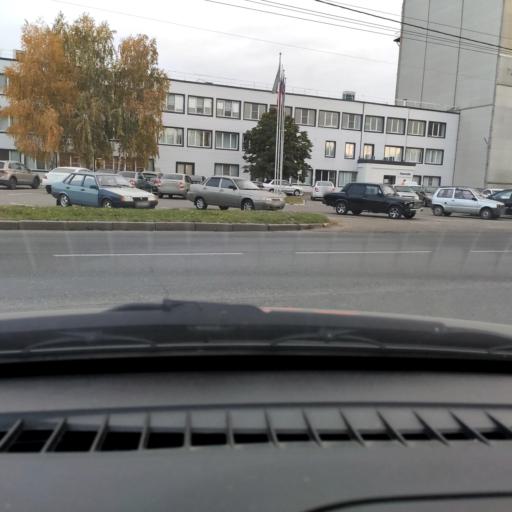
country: RU
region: Samara
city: Tol'yatti
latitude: 53.5603
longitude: 49.2992
